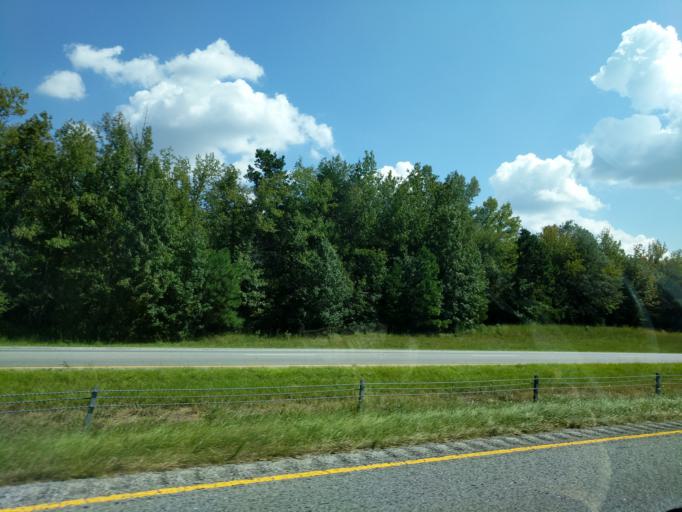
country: US
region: South Carolina
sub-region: Spartanburg County
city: Roebuck
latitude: 34.9044
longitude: -81.9914
